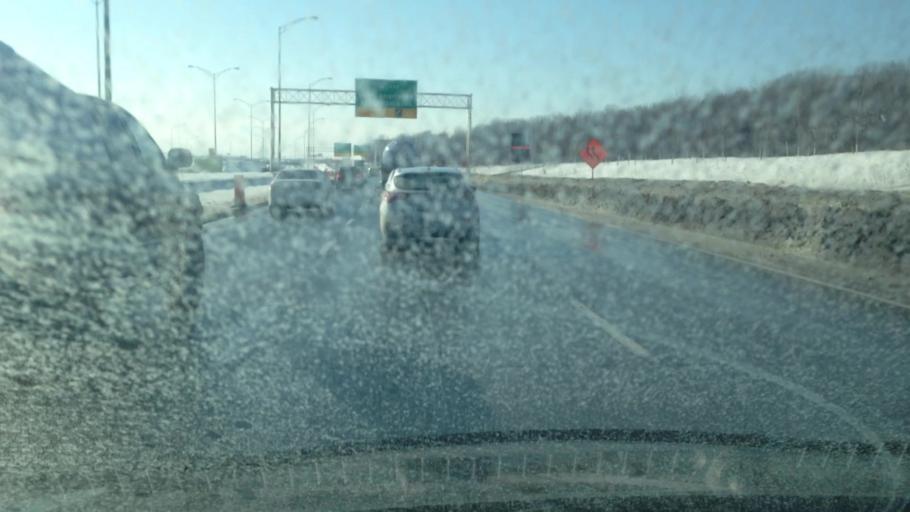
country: CA
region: Quebec
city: Saint-Raymond
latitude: 45.4599
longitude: -73.6191
